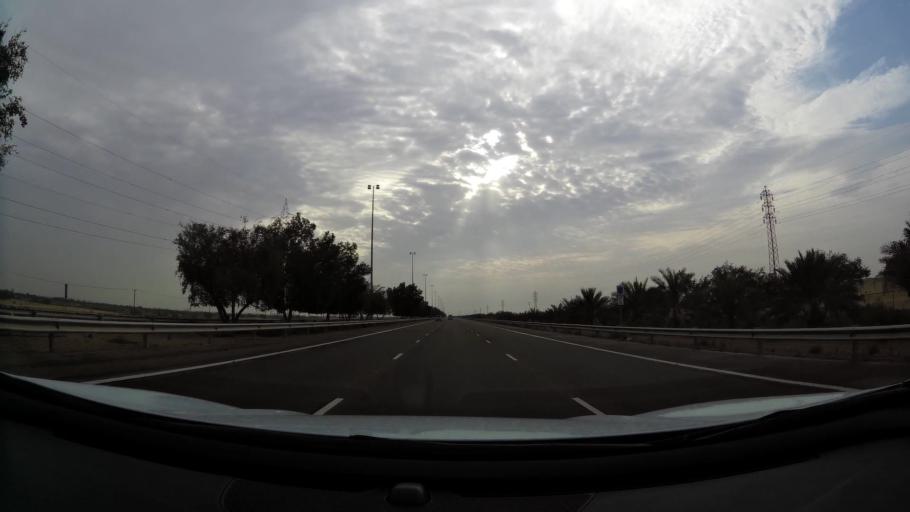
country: AE
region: Abu Dhabi
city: Abu Dhabi
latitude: 24.1985
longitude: 54.9195
